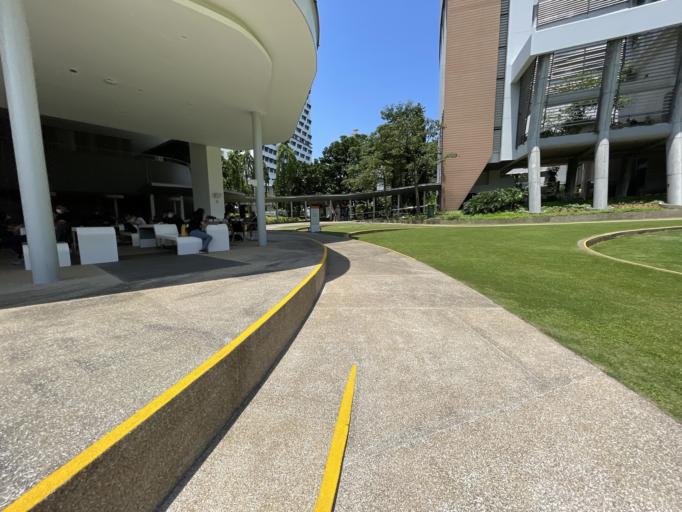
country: SG
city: Singapore
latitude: 1.3053
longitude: 103.7733
